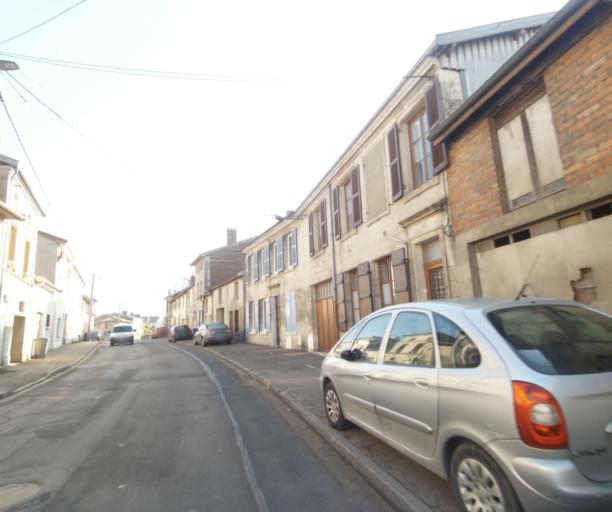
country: FR
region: Champagne-Ardenne
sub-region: Departement de la Haute-Marne
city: Wassy
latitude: 48.4953
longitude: 4.9525
